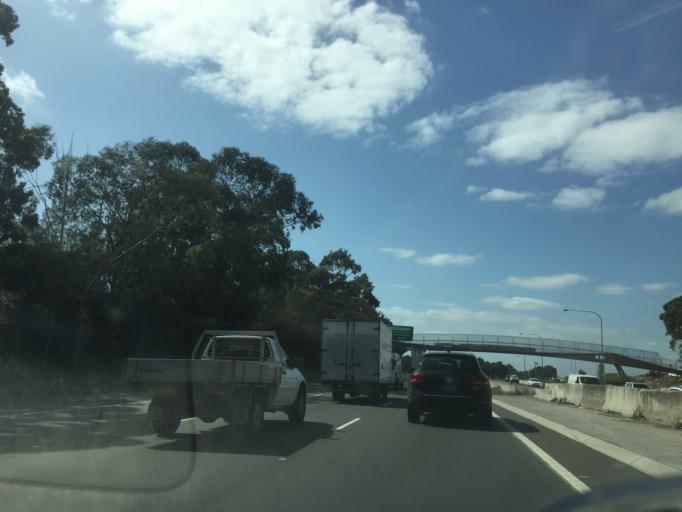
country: AU
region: New South Wales
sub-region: Auburn
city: Auburn
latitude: -33.8403
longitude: 151.0394
